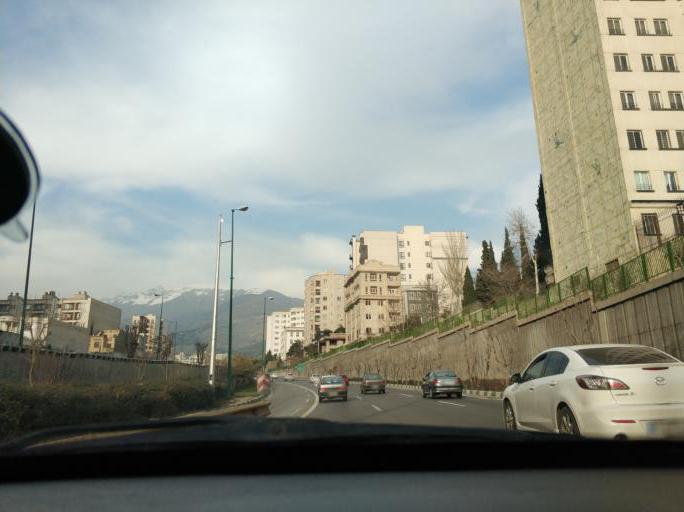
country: IR
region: Tehran
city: Tajrish
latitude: 35.7922
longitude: 51.4920
